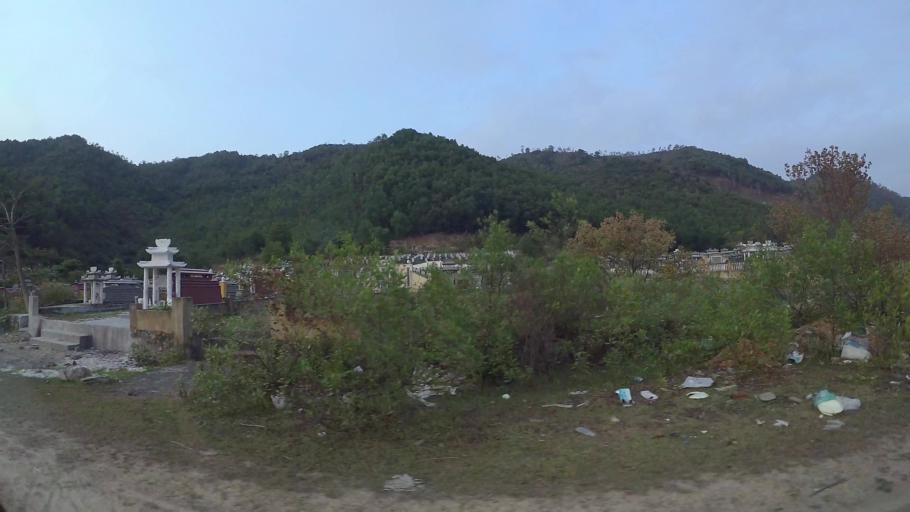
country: VN
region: Da Nang
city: Lien Chieu
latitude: 16.0612
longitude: 108.1225
